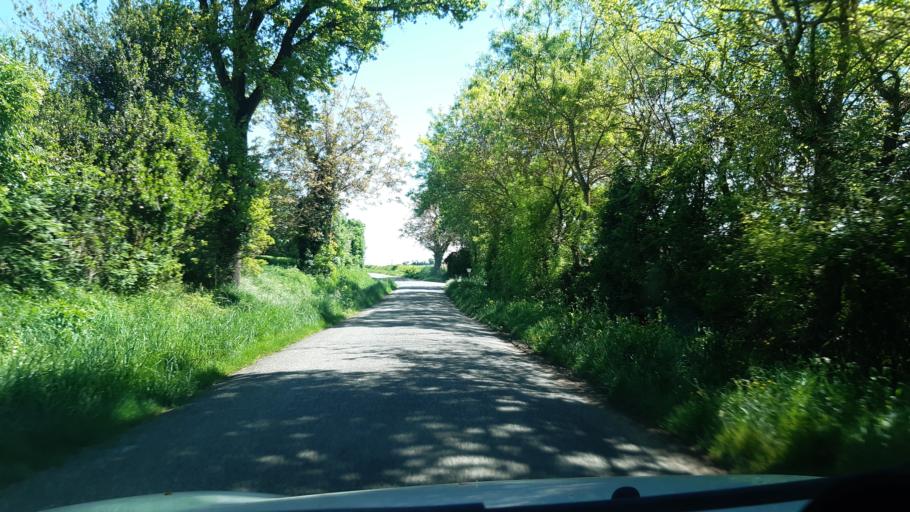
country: FR
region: Midi-Pyrenees
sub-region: Departement du Gers
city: Samatan
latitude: 43.5089
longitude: 1.0138
